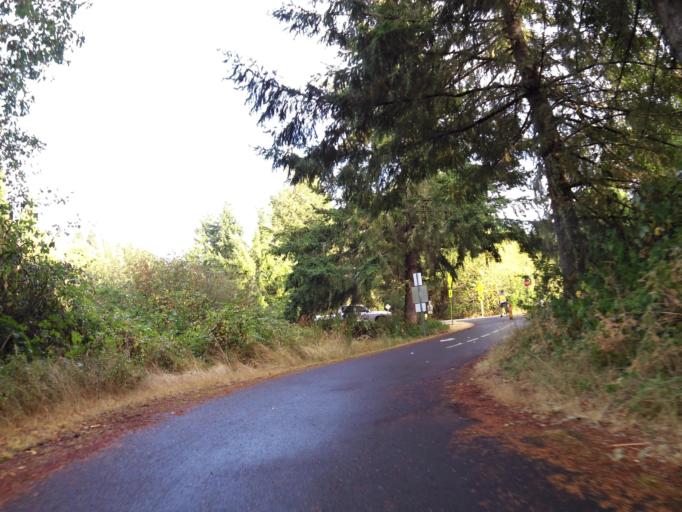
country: US
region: Washington
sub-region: Thurston County
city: Rainier
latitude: 46.9032
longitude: -122.7650
